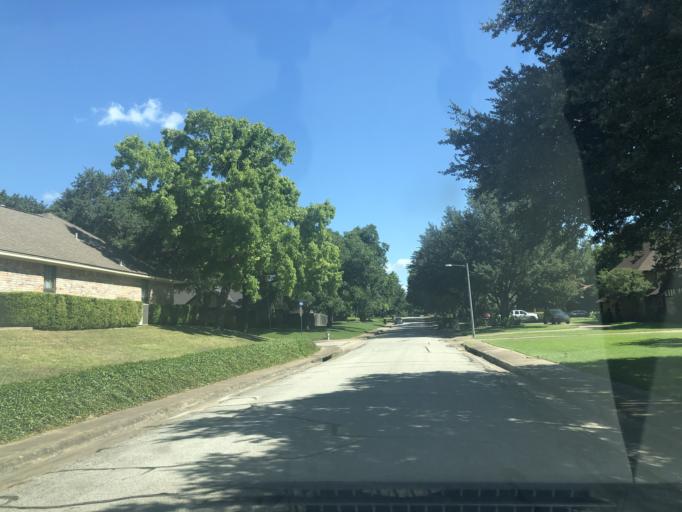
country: US
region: Texas
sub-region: Dallas County
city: Duncanville
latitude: 32.6399
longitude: -96.9267
